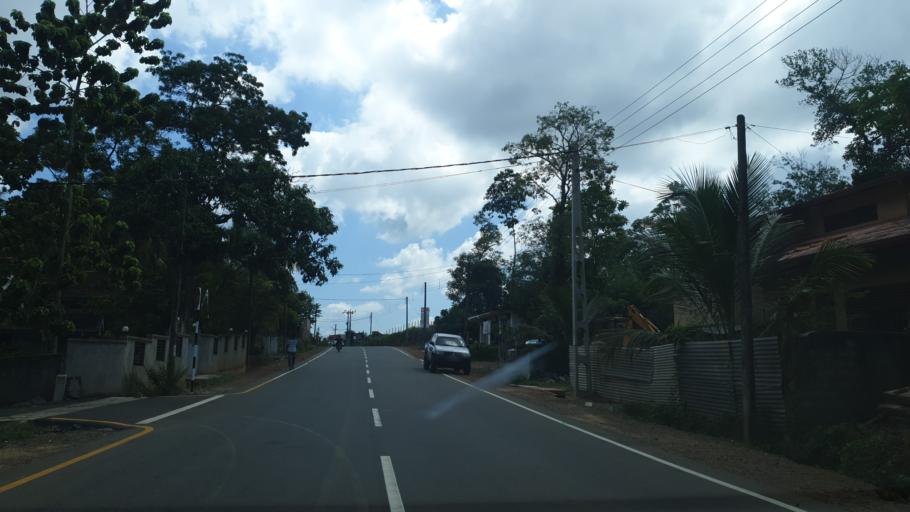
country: LK
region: Western
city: Panadura
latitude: 6.6686
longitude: 79.9461
